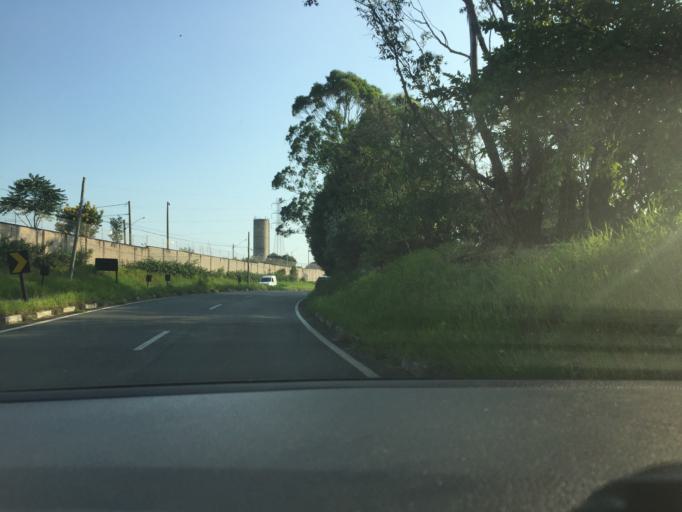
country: BR
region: Sao Paulo
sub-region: Vinhedo
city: Vinhedo
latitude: -23.0166
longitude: -47.0007
